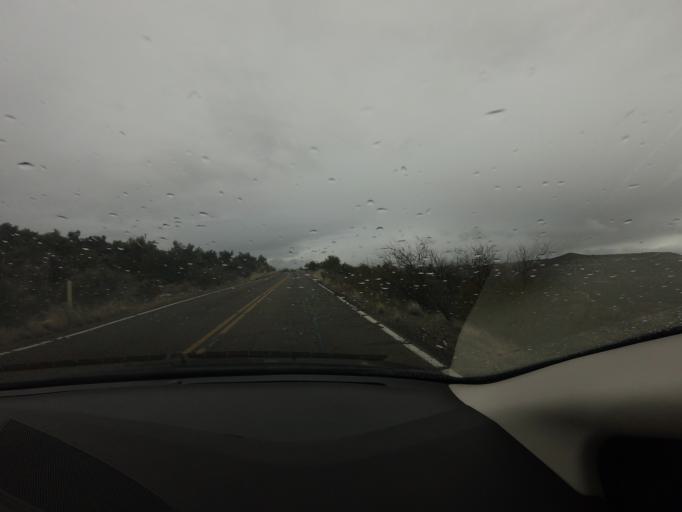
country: US
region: Arizona
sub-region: Yavapai County
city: Camp Verde
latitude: 34.6061
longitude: -111.8551
